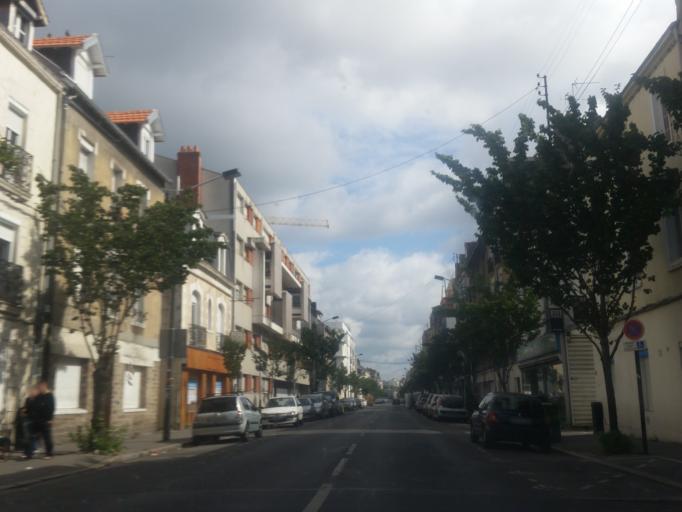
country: FR
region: Pays de la Loire
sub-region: Departement de la Loire-Atlantique
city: Nantes
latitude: 47.2203
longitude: -1.5318
